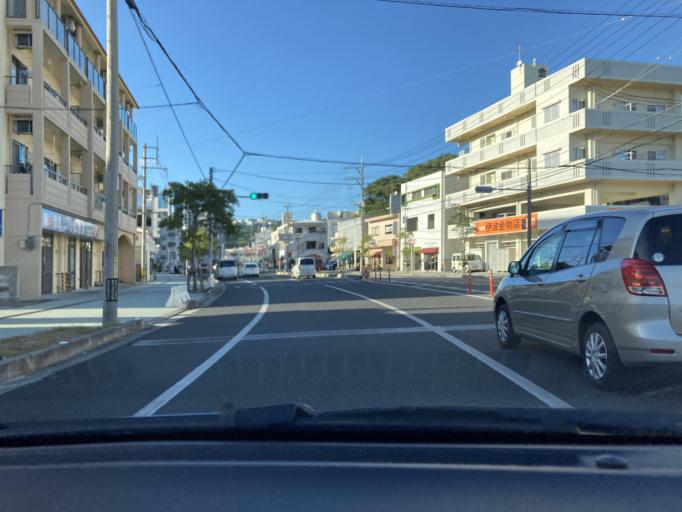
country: JP
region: Okinawa
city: Tomigusuku
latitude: 26.1936
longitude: 127.7279
